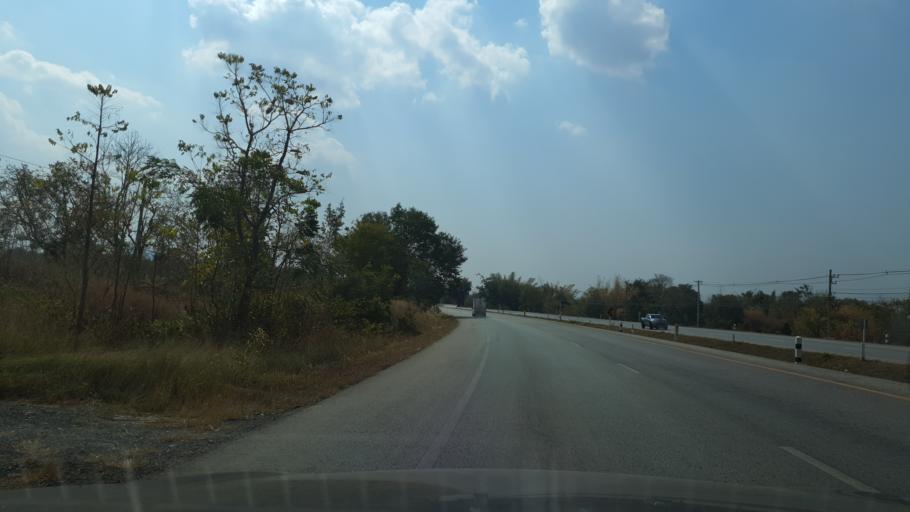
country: TH
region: Lampang
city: Mae Phrik
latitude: 17.4107
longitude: 99.1511
